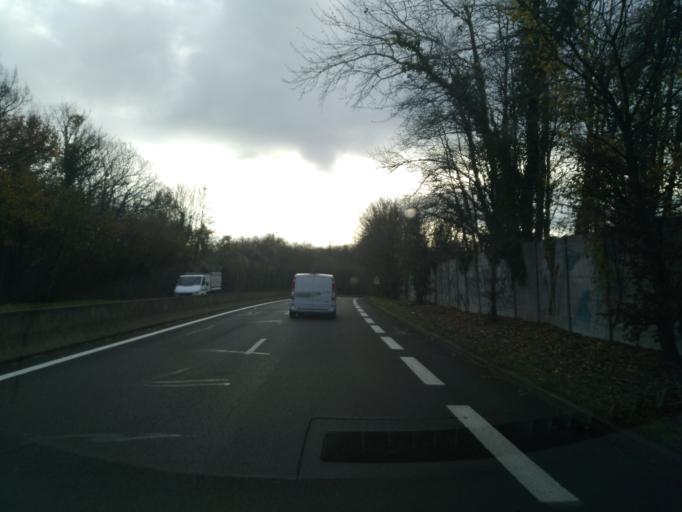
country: FR
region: Ile-de-France
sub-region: Departement des Yvelines
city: Buc
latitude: 48.7816
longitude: 2.1059
